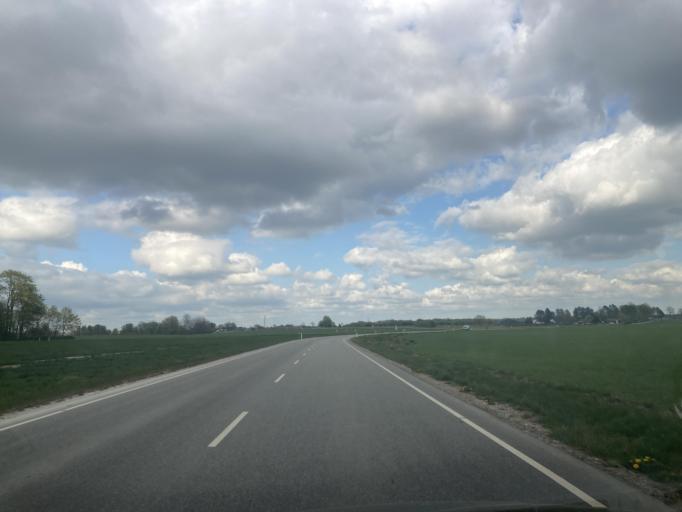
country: DK
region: Zealand
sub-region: Roskilde Kommune
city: Vindinge
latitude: 55.5976
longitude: 12.1159
